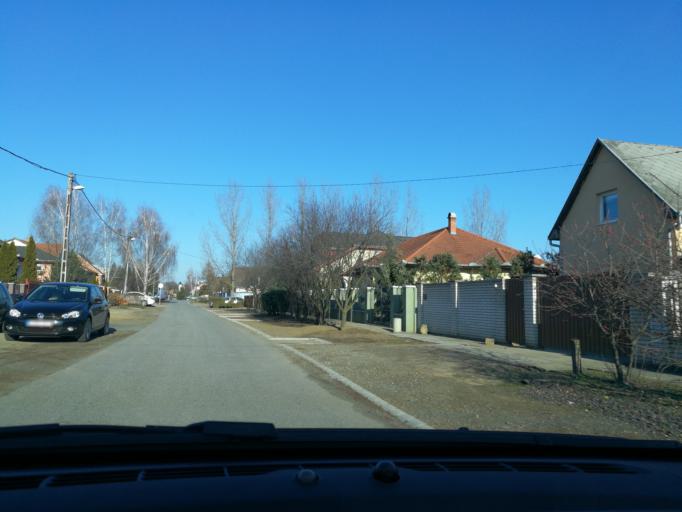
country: HU
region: Szabolcs-Szatmar-Bereg
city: Nyiregyhaza
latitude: 47.9301
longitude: 21.7533
